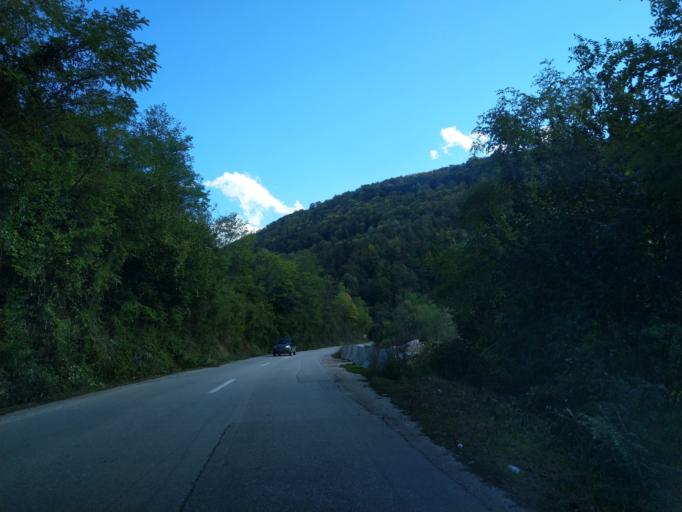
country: RS
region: Central Serbia
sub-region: Zlatiborski Okrug
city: Uzice
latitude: 43.8812
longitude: 19.7787
